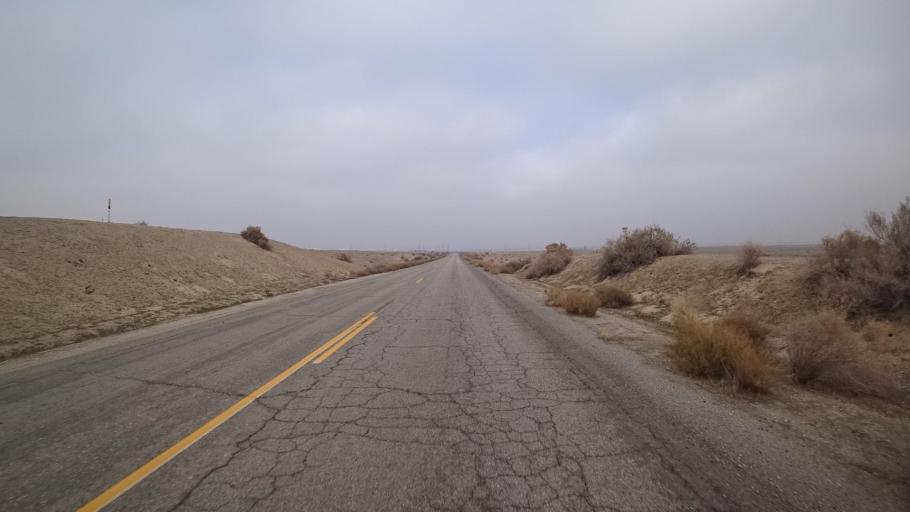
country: US
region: California
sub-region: Kern County
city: Maricopa
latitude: 35.1457
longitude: -119.3399
